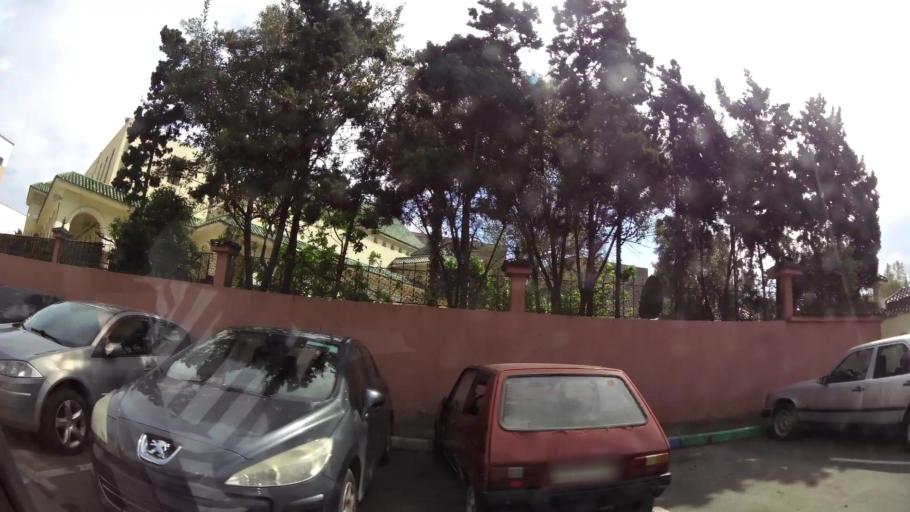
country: MA
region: Grand Casablanca
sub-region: Casablanca
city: Casablanca
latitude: 33.5781
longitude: -7.5847
